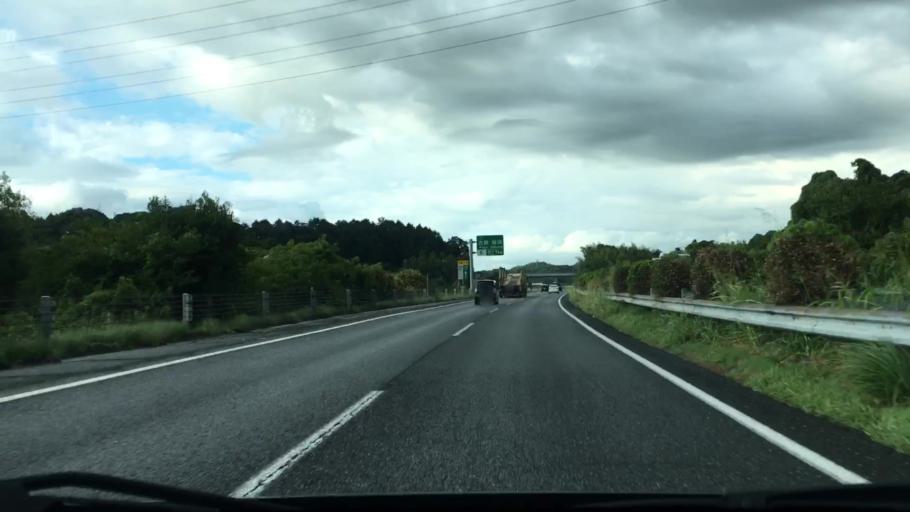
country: JP
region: Fukuoka
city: Koga
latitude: 33.7077
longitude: 130.4867
